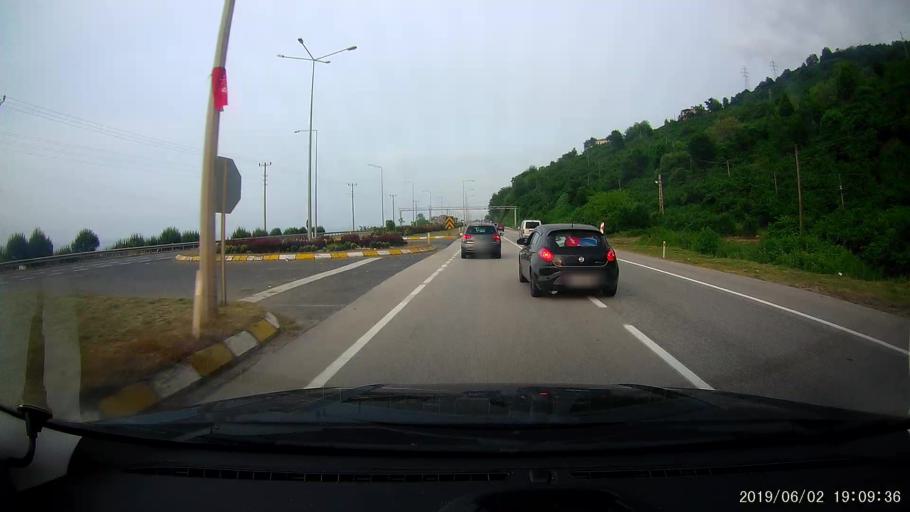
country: TR
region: Ordu
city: Gulyali
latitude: 40.9725
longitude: 38.0309
